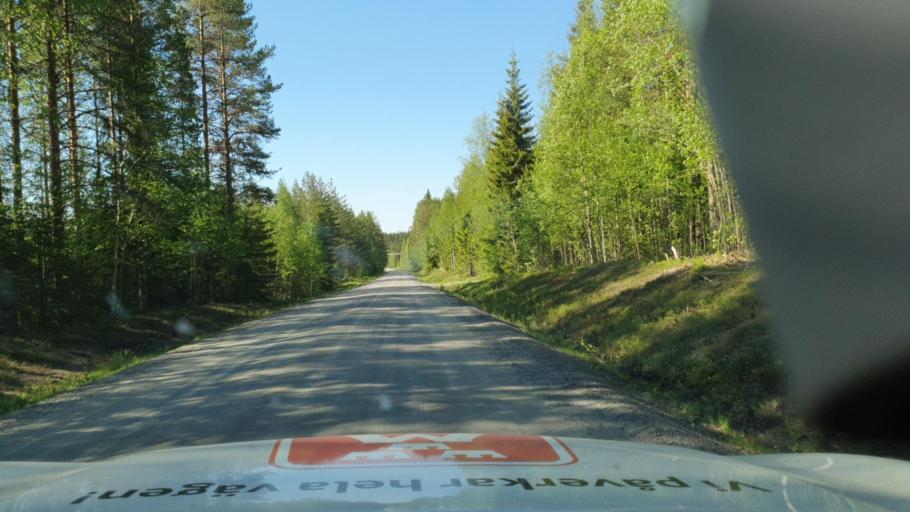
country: SE
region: Vaesterbotten
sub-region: Vannas Kommun
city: Vaennaes
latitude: 64.0098
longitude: 19.7349
